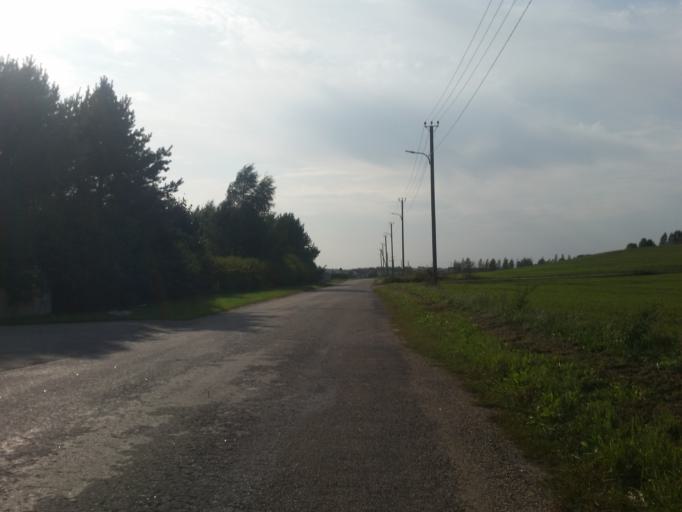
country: LV
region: Ikskile
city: Ikskile
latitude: 56.8186
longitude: 24.5245
